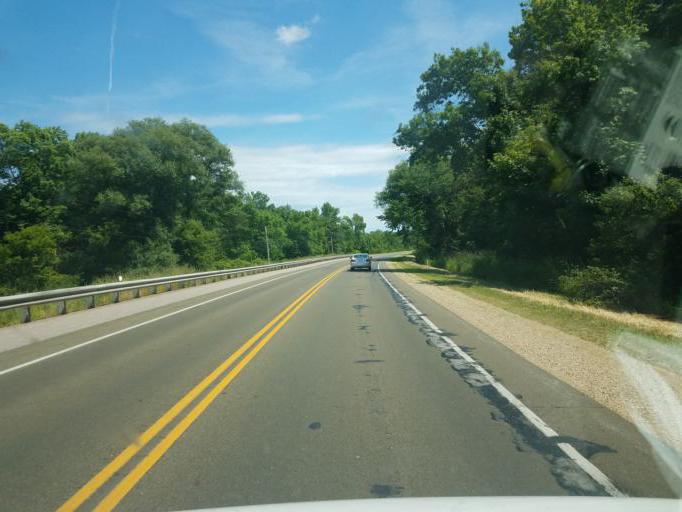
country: US
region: Wisconsin
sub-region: Sauk County
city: Reedsburg
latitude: 43.5610
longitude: -90.0715
